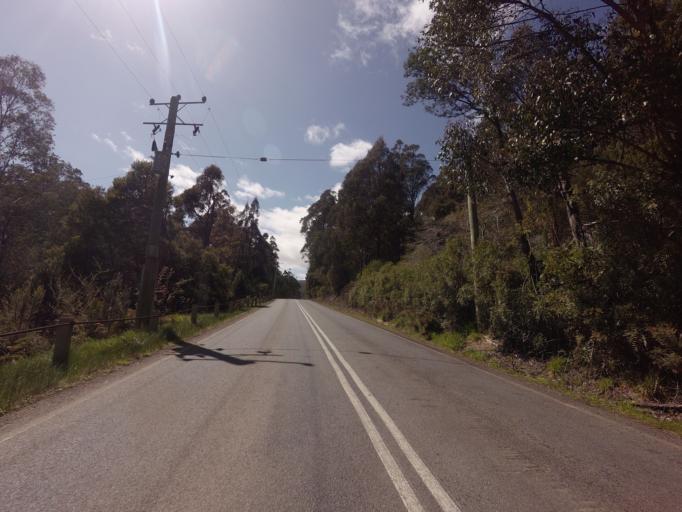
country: AU
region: Tasmania
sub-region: Derwent Valley
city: New Norfolk
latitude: -42.7136
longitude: 146.6955
